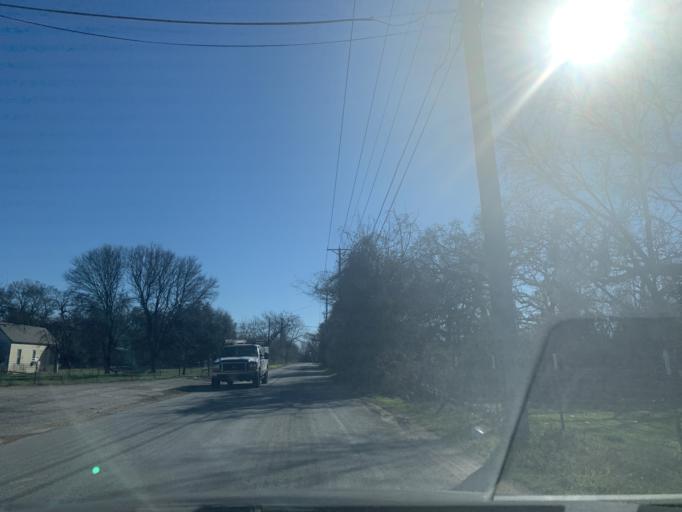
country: US
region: Texas
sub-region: Tarrant County
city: Haltom City
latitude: 32.7722
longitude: -97.2797
